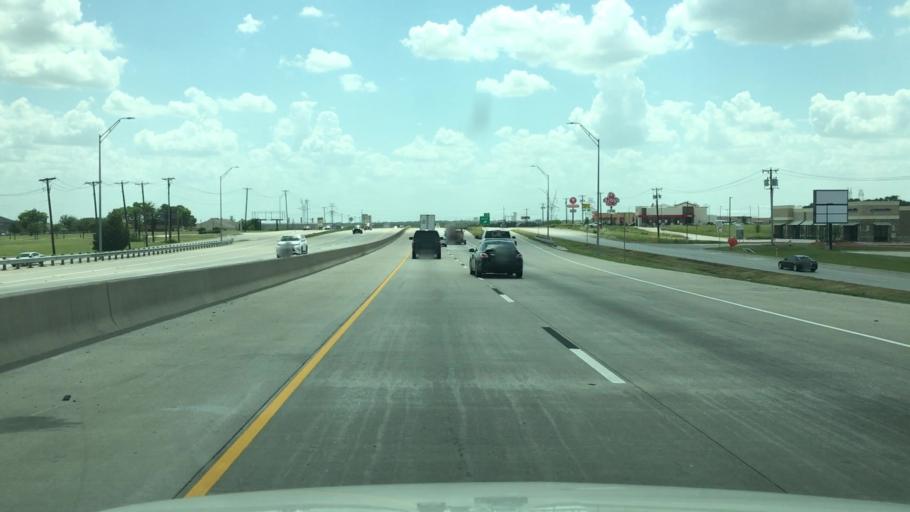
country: US
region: Texas
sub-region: Rockwall County
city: Royse City
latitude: 32.9632
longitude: -96.3423
